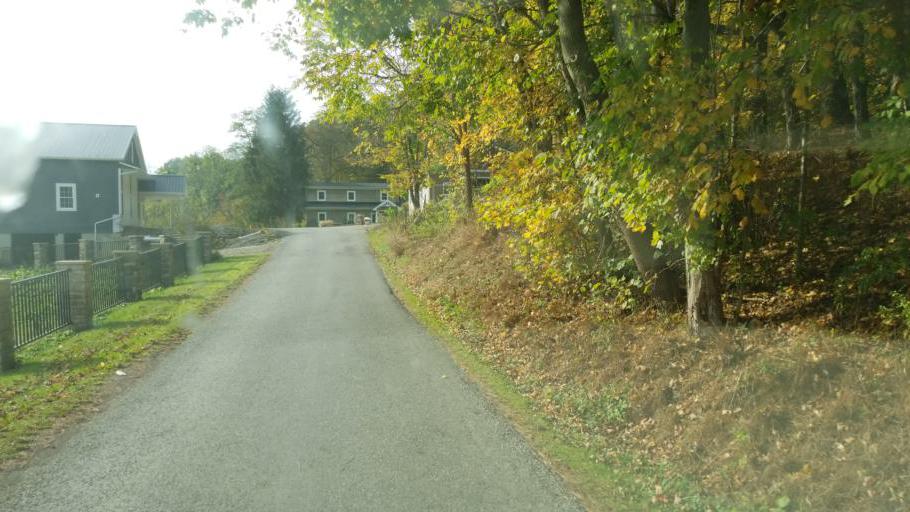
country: US
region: Ohio
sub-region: Holmes County
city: Millersburg
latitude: 40.5328
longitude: -81.8582
